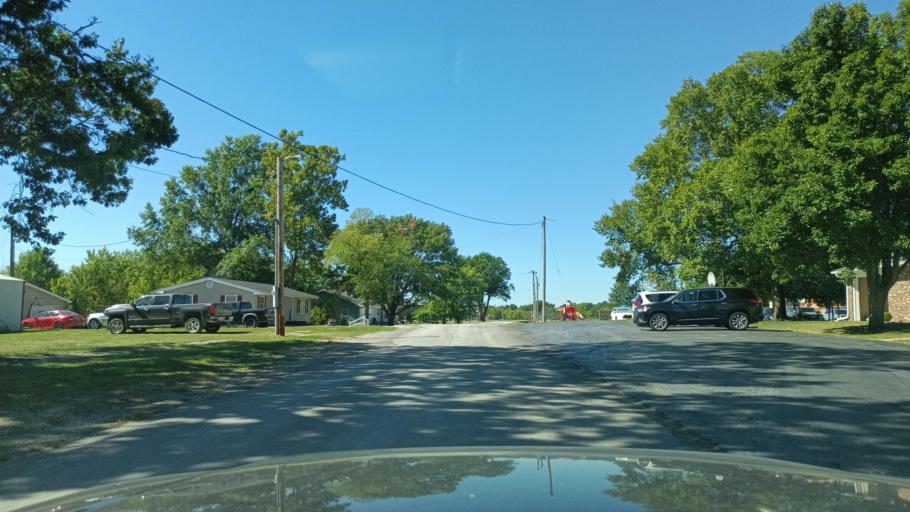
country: US
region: Missouri
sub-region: Macon County
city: La Plata
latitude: 40.0223
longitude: -92.4946
